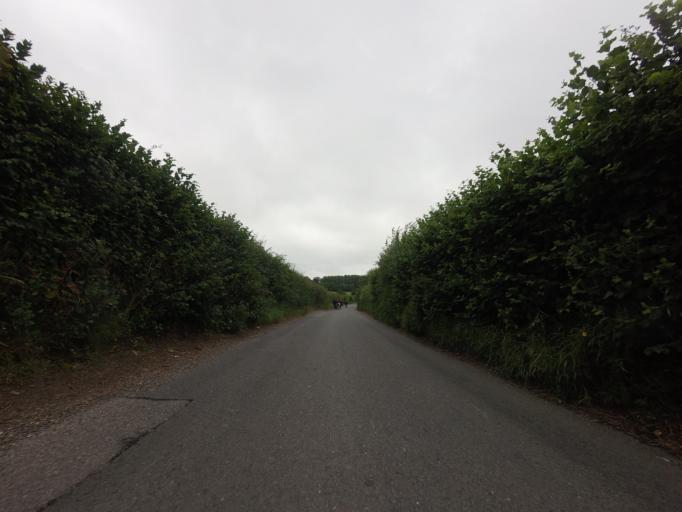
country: GB
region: England
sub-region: Kent
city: Borough Green
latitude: 51.3081
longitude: 0.2827
